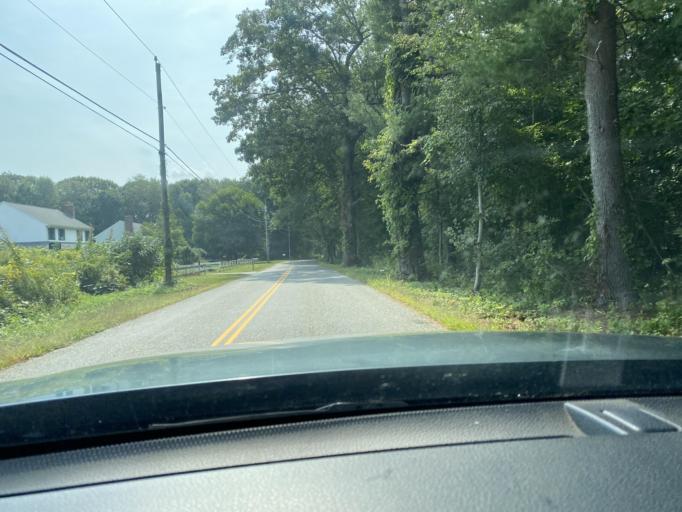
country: US
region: Connecticut
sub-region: New London County
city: Colchester
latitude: 41.6263
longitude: -72.3043
